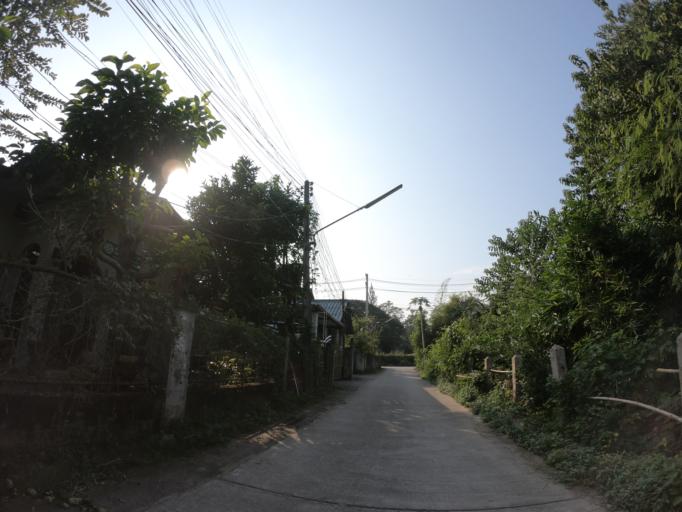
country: TH
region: Chiang Mai
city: Chiang Mai
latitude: 18.7694
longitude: 99.0084
